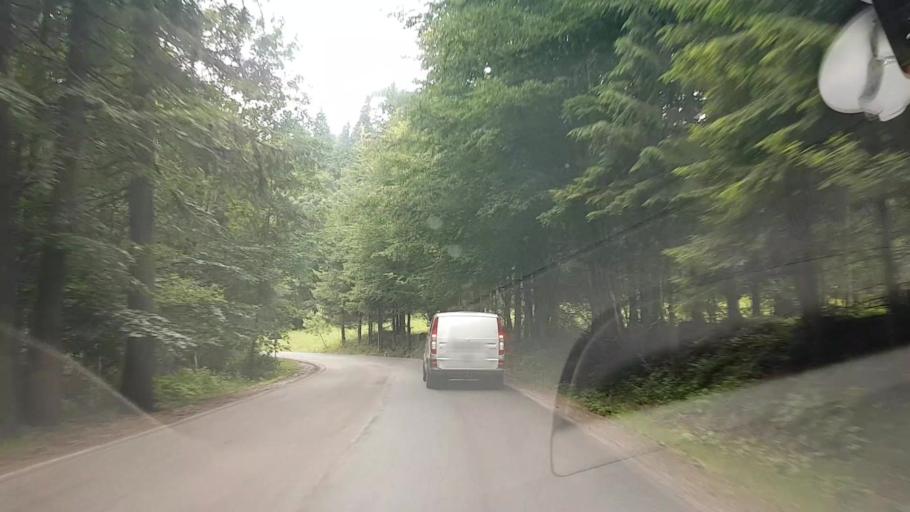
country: RO
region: Harghita
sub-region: Comuna Varsag
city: Varsag
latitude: 46.6652
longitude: 25.3191
